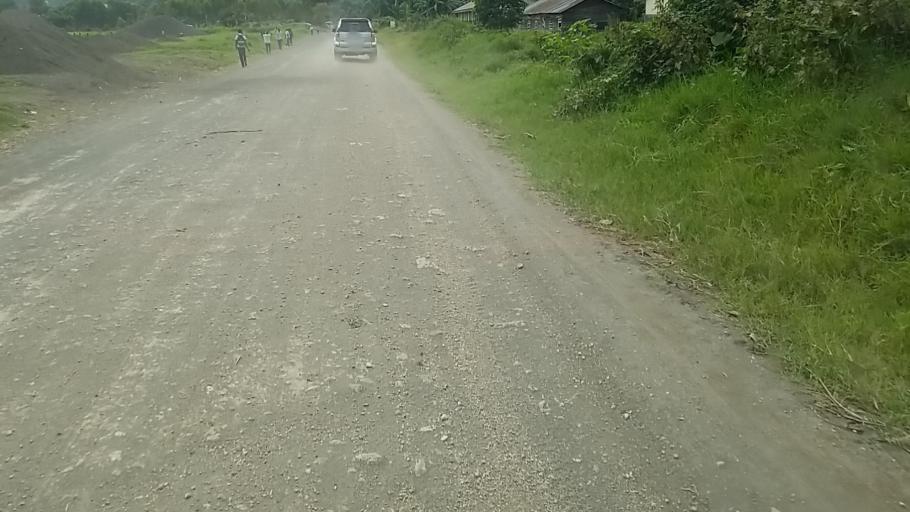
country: CD
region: Nord Kivu
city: Sake
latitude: -1.5681
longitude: 29.0439
